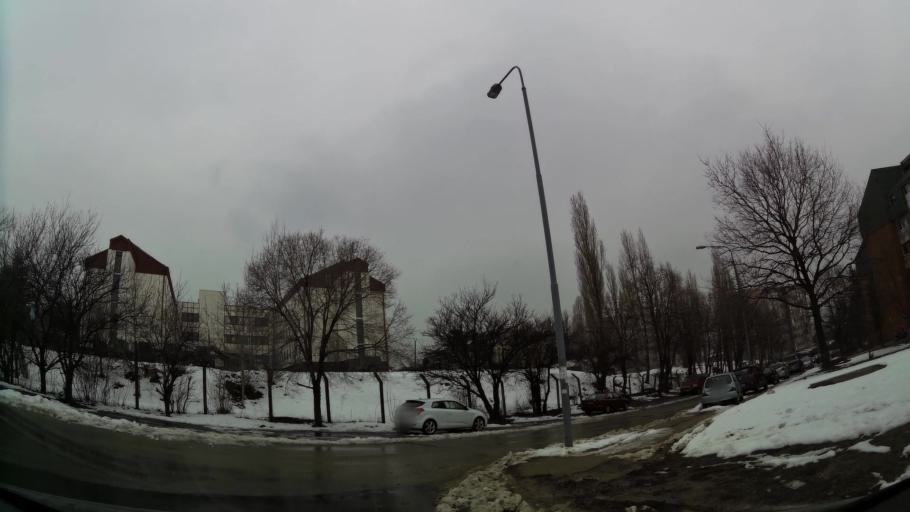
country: RS
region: Central Serbia
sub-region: Belgrade
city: Vozdovac
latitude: 44.7519
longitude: 20.4986
